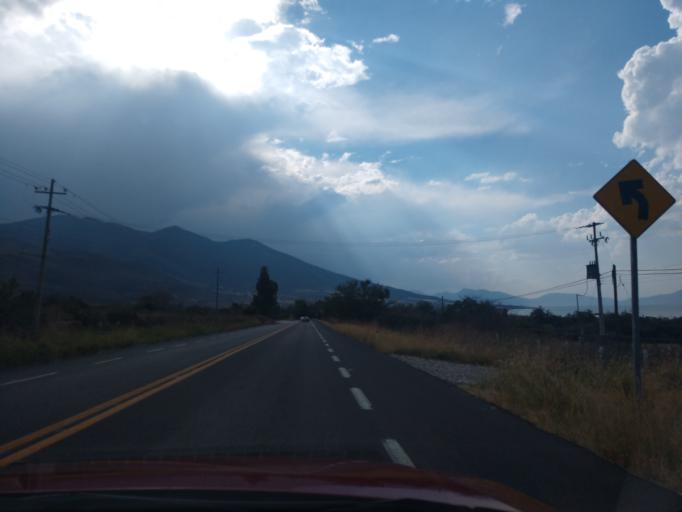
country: MX
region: Jalisco
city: San Juan Cosala
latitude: 20.1942
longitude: -103.2834
